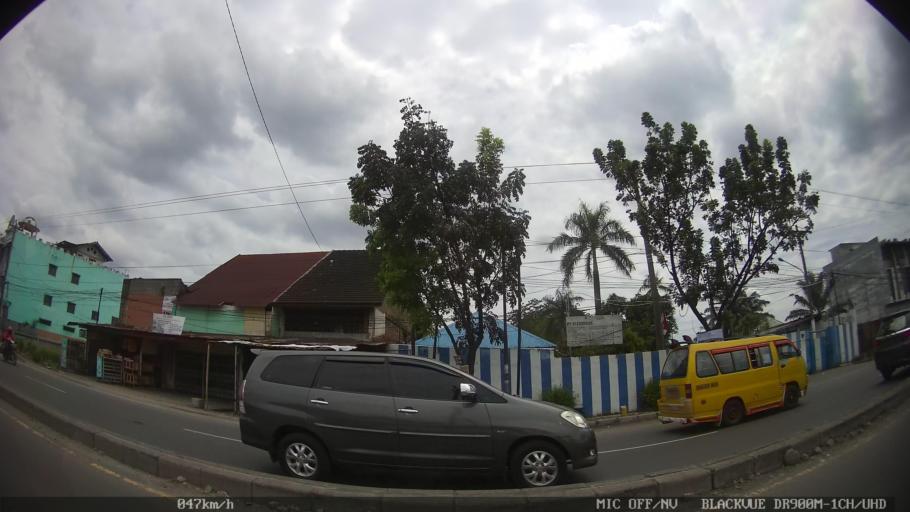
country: ID
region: North Sumatra
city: Sunggal
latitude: 3.5985
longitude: 98.6020
